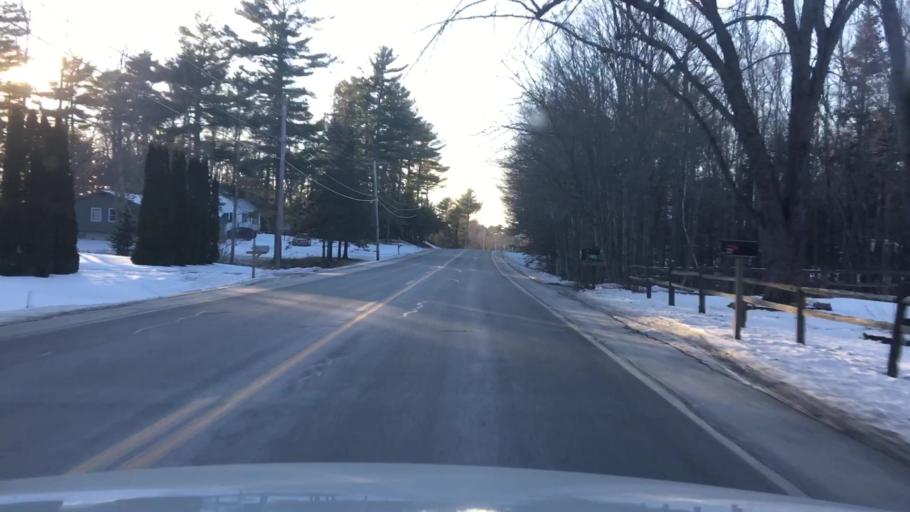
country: US
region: Maine
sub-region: Penobscot County
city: Eddington
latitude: 44.8283
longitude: -68.6809
